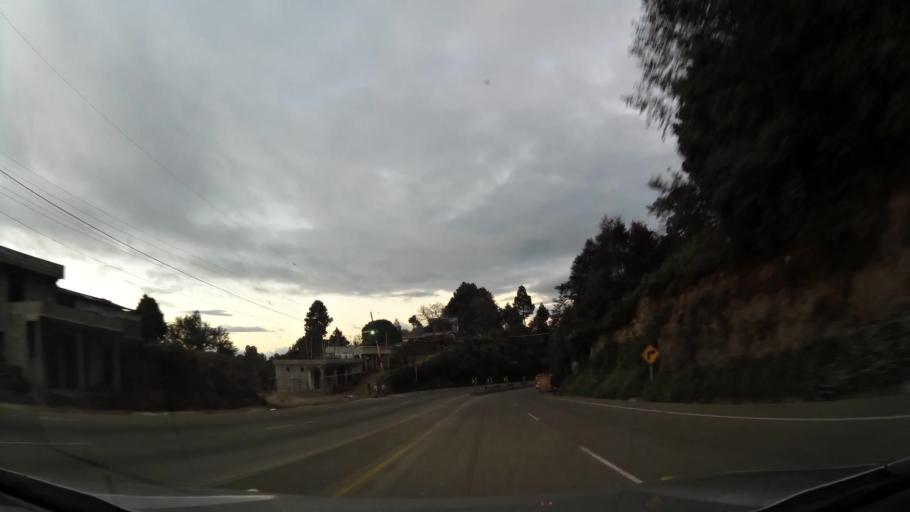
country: GT
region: Quiche
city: Chichicastenango
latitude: 14.8591
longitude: -91.0591
